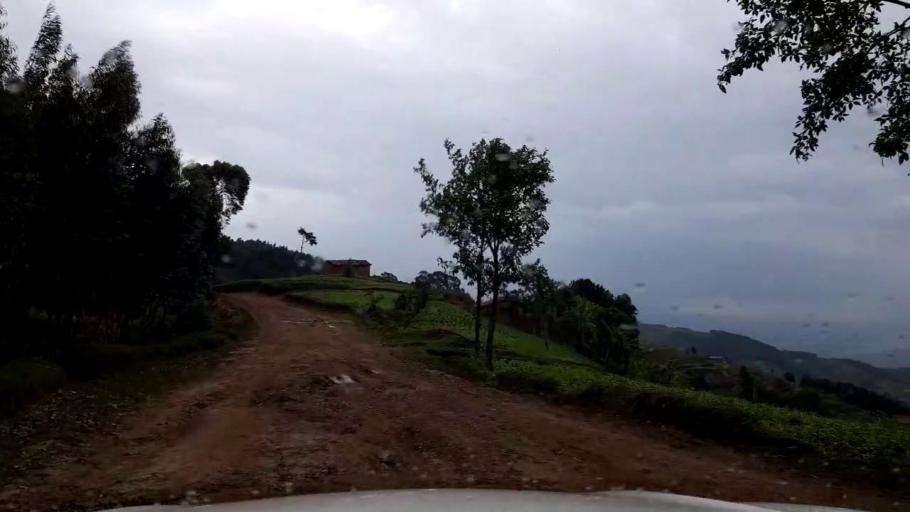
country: RW
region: Western Province
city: Kibuye
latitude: -2.0164
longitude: 29.4660
